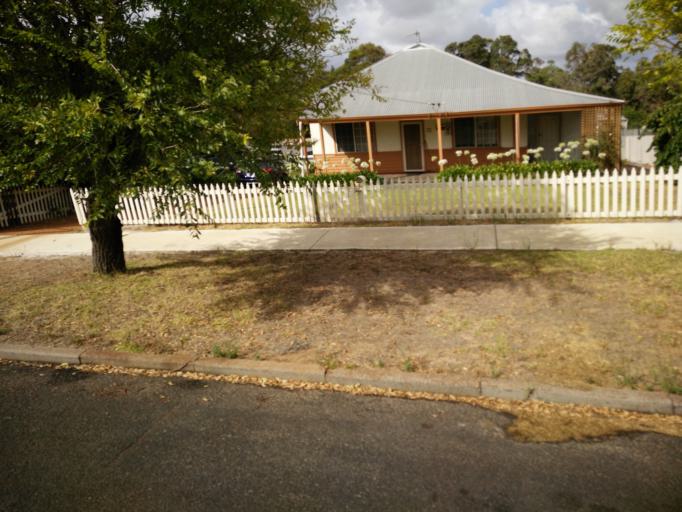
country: AU
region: Western Australia
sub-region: Manjimup
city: Manjimup
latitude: -34.2426
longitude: 116.1406
